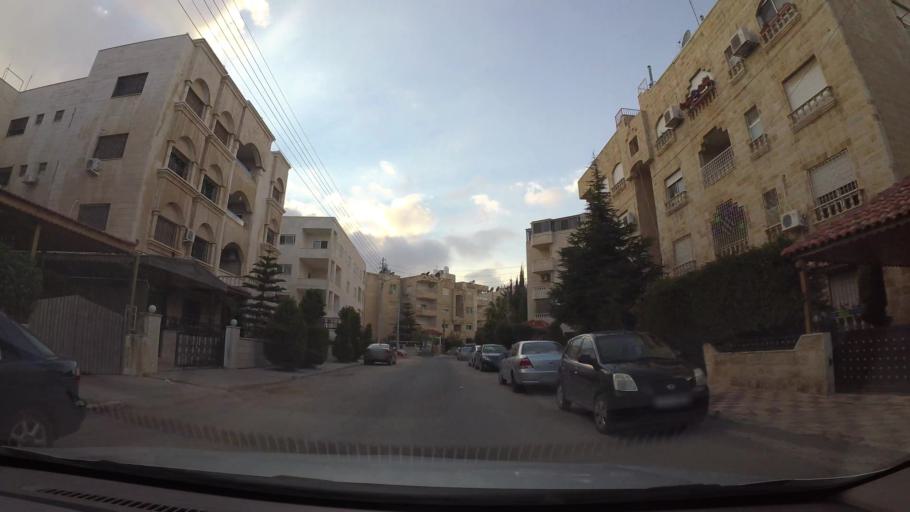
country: JO
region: Amman
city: Al Jubayhah
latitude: 31.9837
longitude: 35.8632
